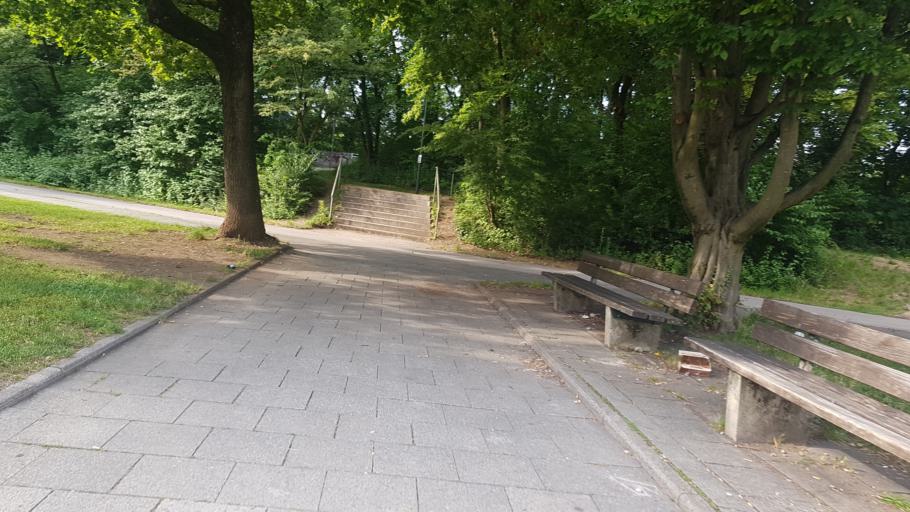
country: DE
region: Bavaria
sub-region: Upper Bavaria
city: Neuried
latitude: 48.1003
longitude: 11.5030
